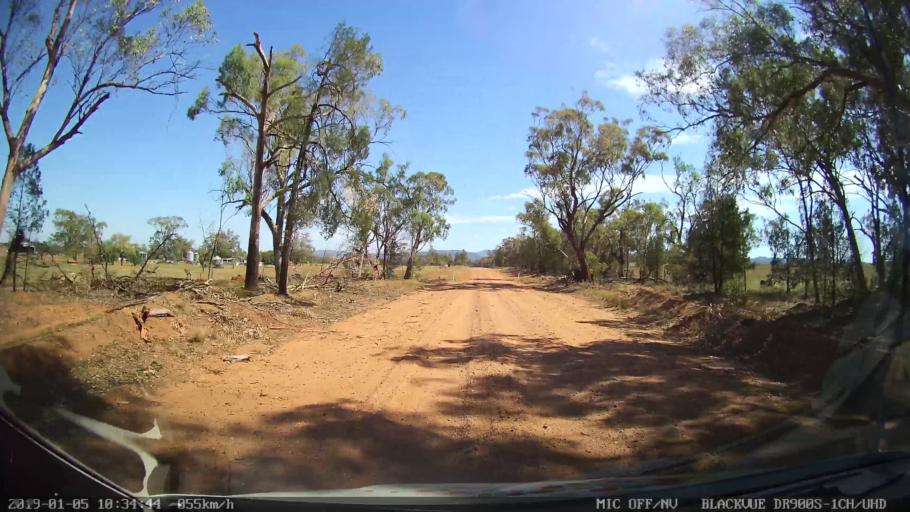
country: AU
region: New South Wales
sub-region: Gilgandra
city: Gilgandra
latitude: -31.4960
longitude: 148.9293
